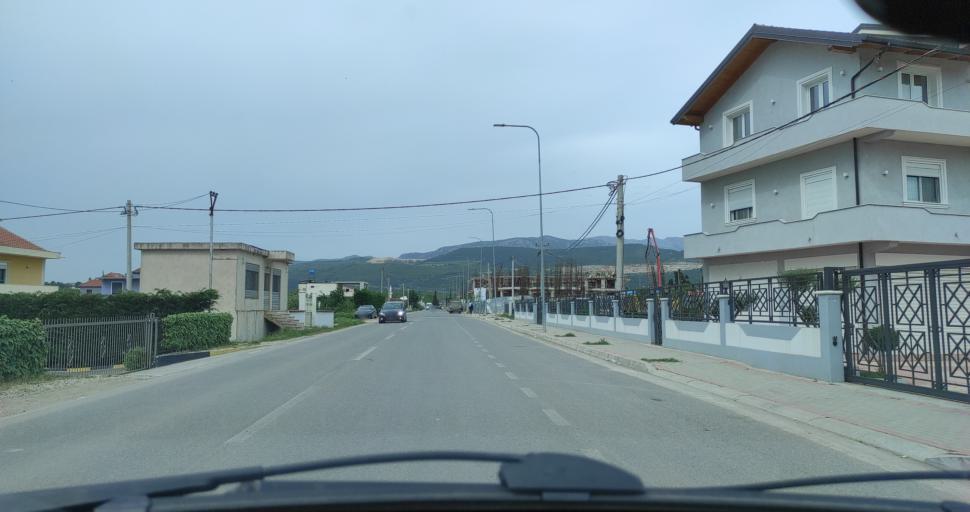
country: AL
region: Durres
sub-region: Rrethi i Krujes
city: Fushe-Kruje
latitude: 41.4837
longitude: 19.7241
